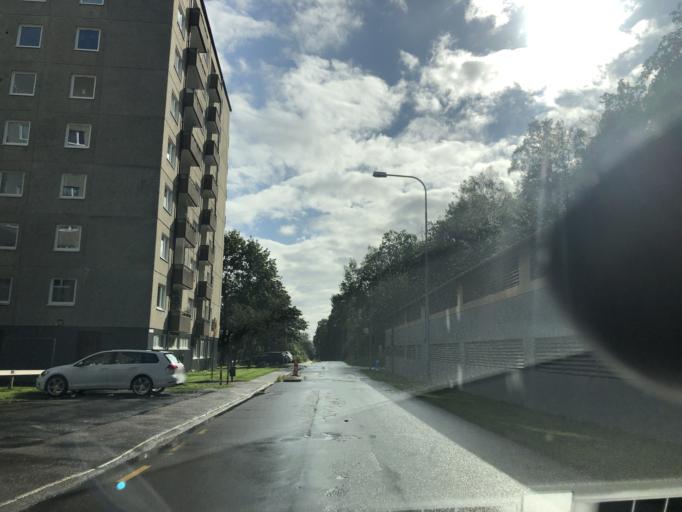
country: SE
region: Vaestra Goetaland
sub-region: Goteborg
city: Goeteborg
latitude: 57.7339
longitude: 11.9707
